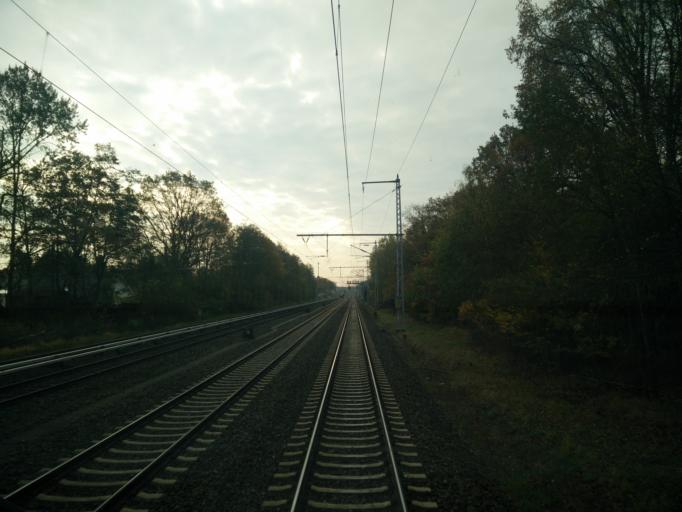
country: DE
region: Brandenburg
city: Zeuthen
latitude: 52.3789
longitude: 13.6102
